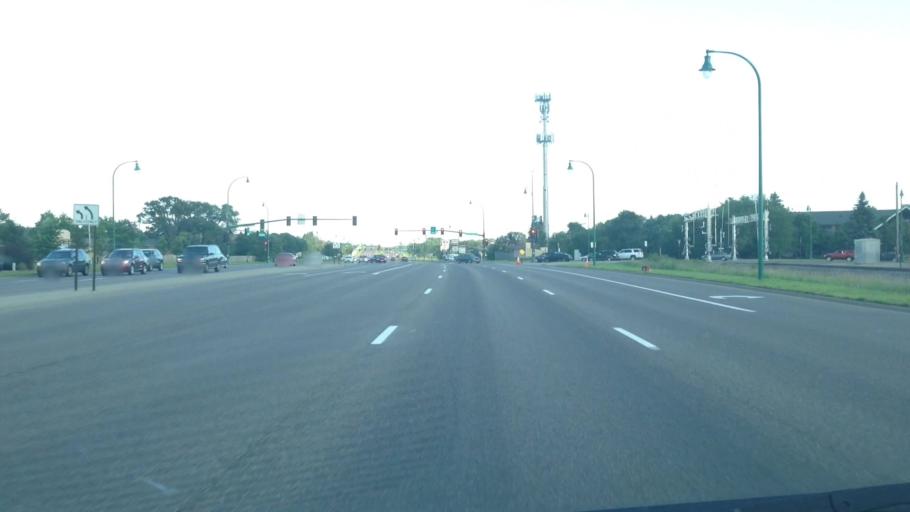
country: US
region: Minnesota
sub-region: Hennepin County
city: Crystal
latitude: 45.0558
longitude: -93.3593
